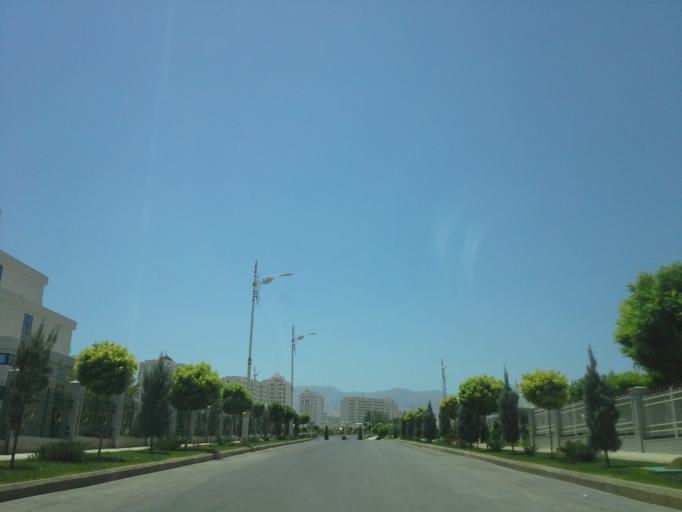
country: TM
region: Ahal
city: Ashgabat
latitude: 37.9300
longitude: 58.3708
